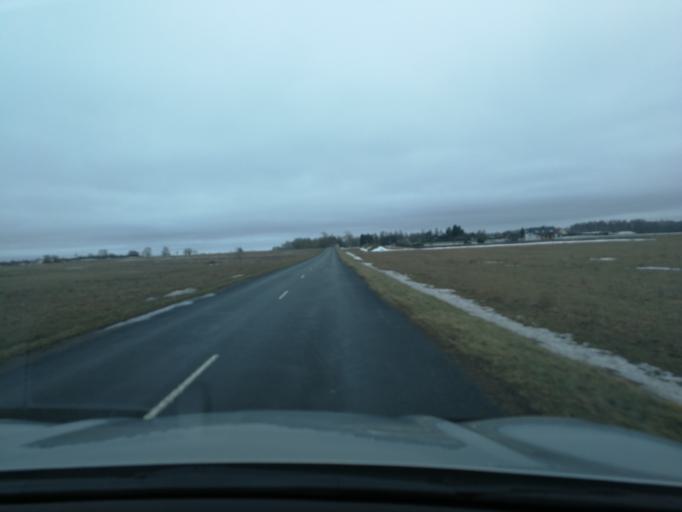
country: EE
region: Harju
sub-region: Kiili vald
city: Kiili
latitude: 59.2811
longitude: 24.8752
